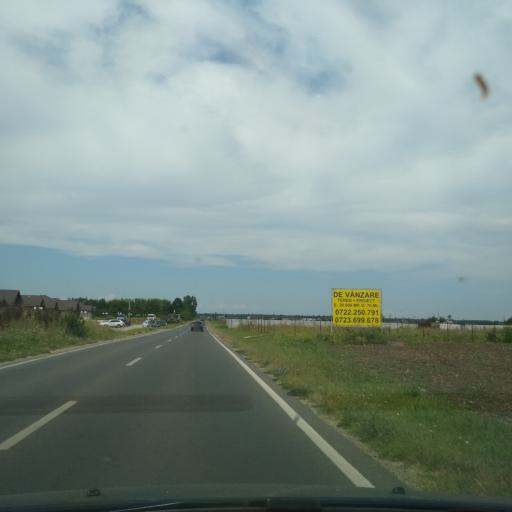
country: RO
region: Ilfov
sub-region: Comuna Balotesti
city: Balotesti
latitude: 44.6041
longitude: 26.1310
